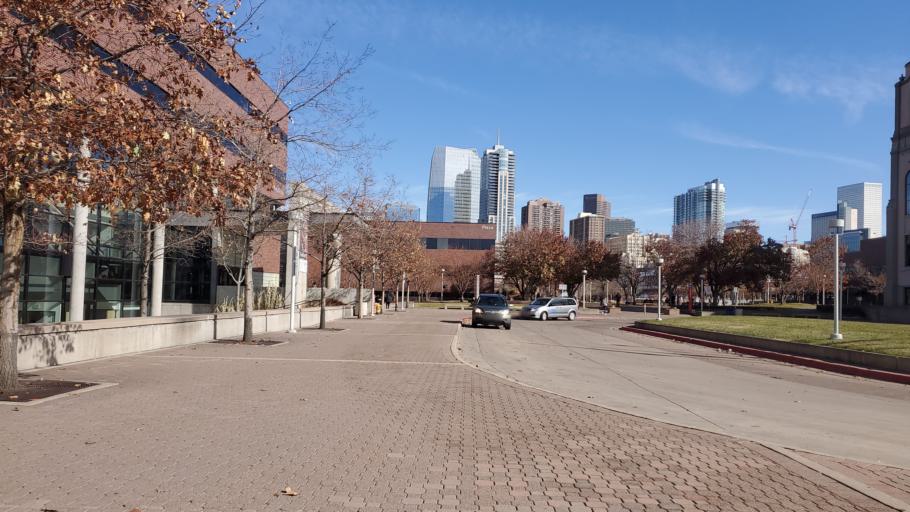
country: US
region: Colorado
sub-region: Denver County
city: Denver
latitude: 39.7431
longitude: -105.0061
